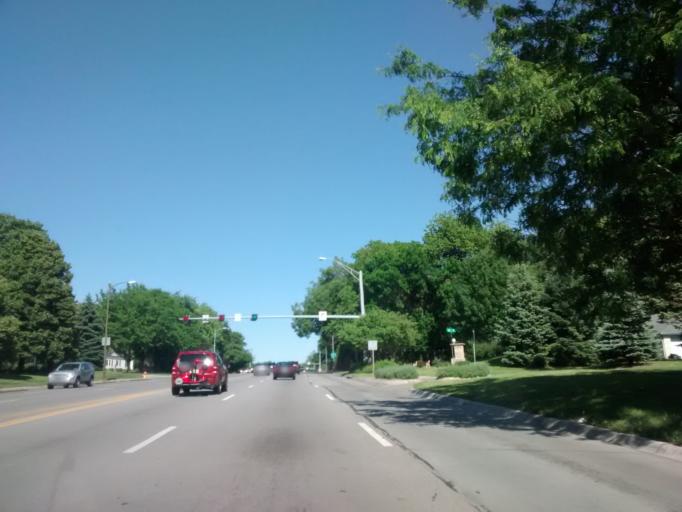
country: US
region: Nebraska
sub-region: Douglas County
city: Ralston
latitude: 41.2594
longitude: -96.0184
